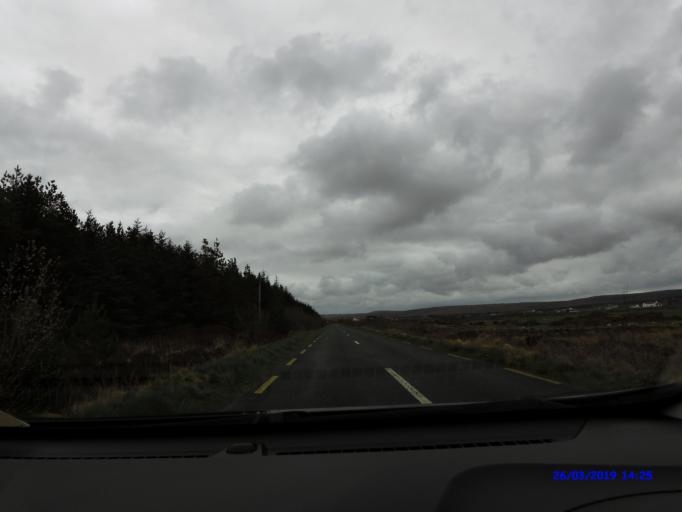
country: IE
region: Connaught
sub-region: Maigh Eo
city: Belmullet
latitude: 54.2407
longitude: -9.6623
